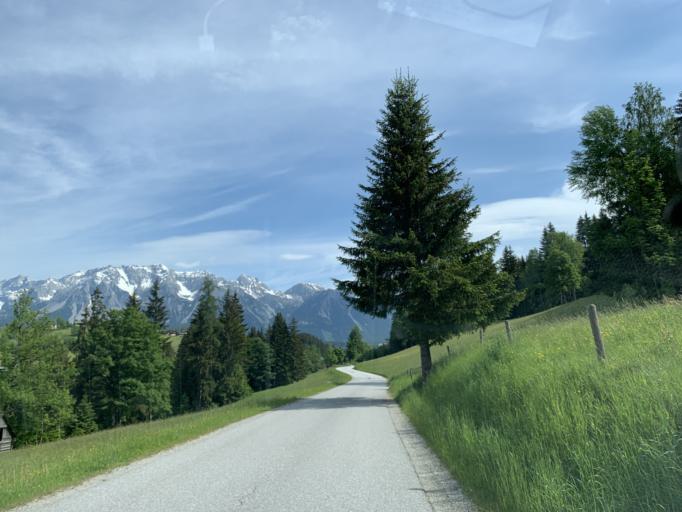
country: AT
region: Styria
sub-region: Politischer Bezirk Liezen
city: Schladming
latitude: 47.3644
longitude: 13.6695
